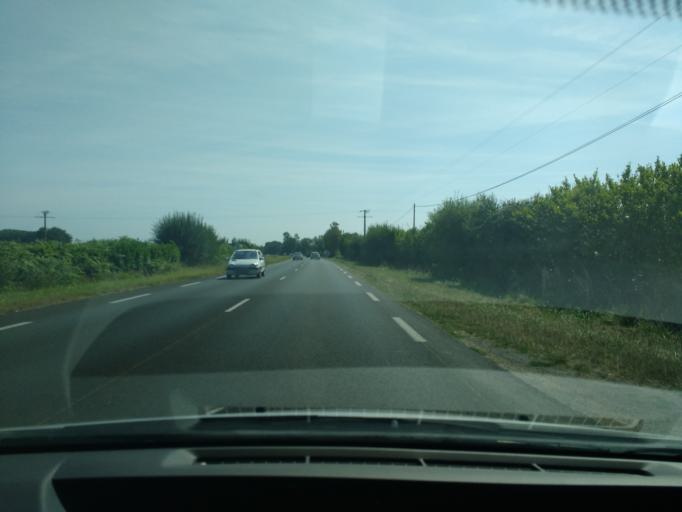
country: FR
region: Pays de la Loire
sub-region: Departement de Maine-et-Loire
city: Andard
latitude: 47.4655
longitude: -0.4239
